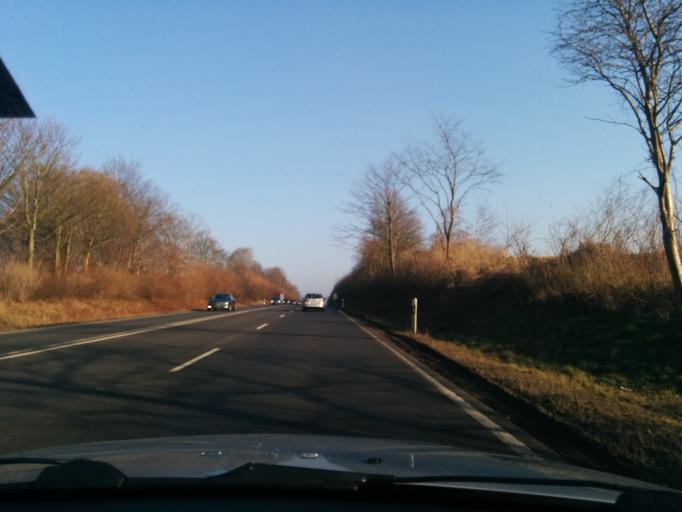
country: DE
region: Hesse
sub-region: Regierungsbezirk Kassel
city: Kaufungen
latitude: 51.2785
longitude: 9.6047
